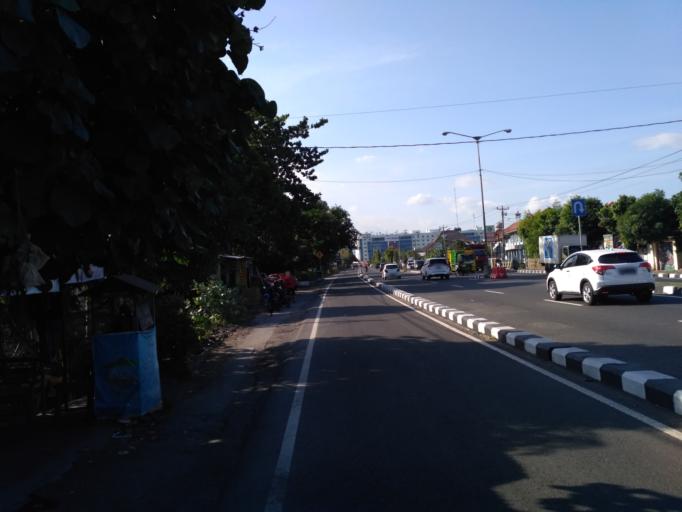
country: ID
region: Daerah Istimewa Yogyakarta
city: Depok
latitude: -7.7716
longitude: 110.4309
